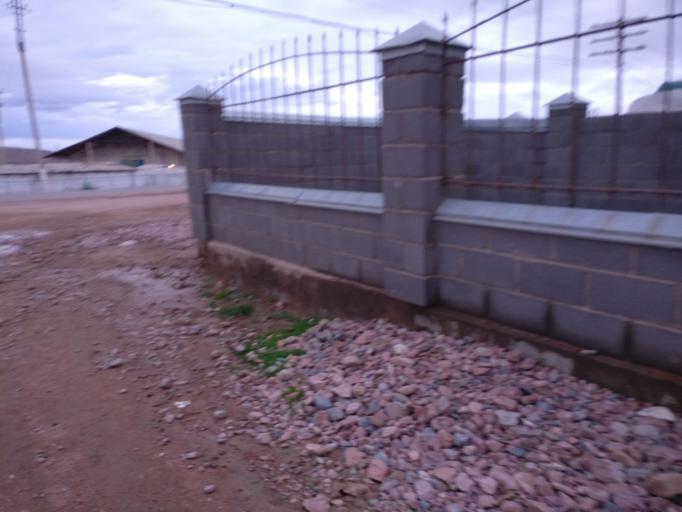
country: KG
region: Ysyk-Koel
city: Bokombayevskoye
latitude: 42.1153
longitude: 76.9822
